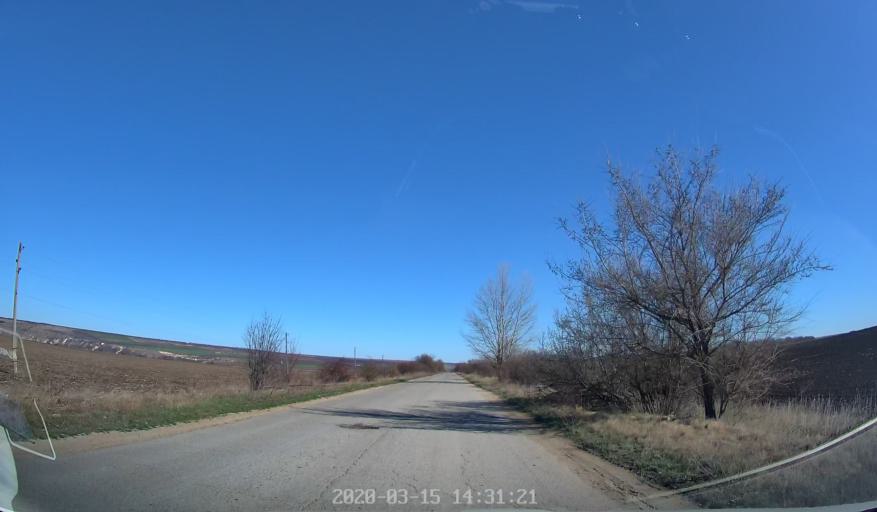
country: MD
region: Orhei
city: Orhei
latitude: 47.3450
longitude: 28.8945
